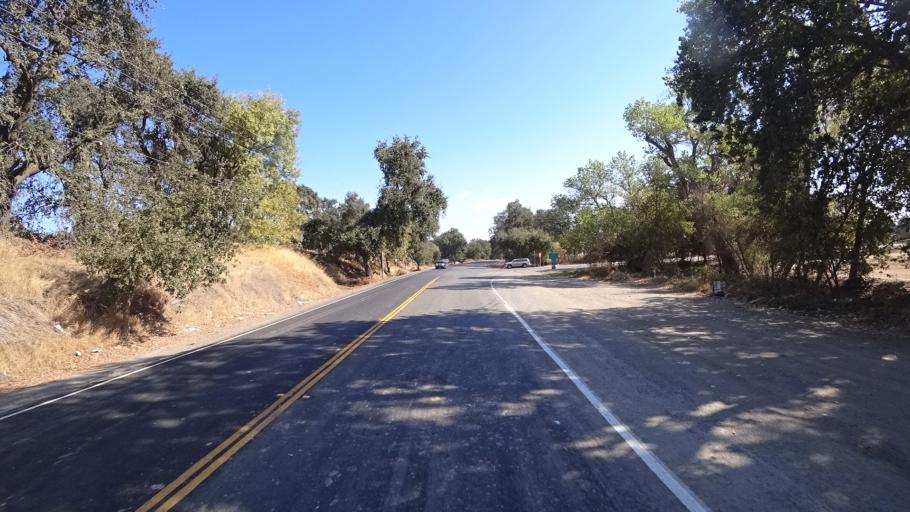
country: US
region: California
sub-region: Yolo County
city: Woodland
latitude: 38.6766
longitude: -121.6383
